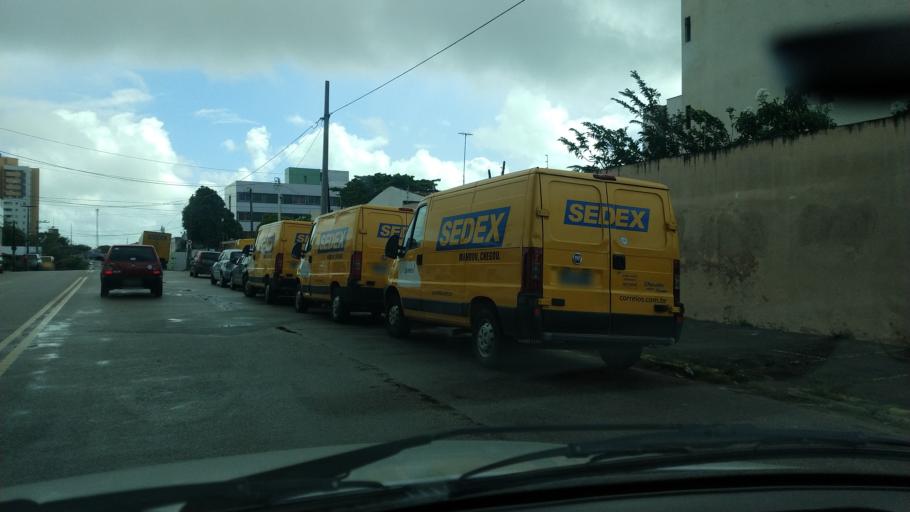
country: BR
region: Rio Grande do Norte
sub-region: Natal
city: Natal
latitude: -5.8121
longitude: -35.2190
